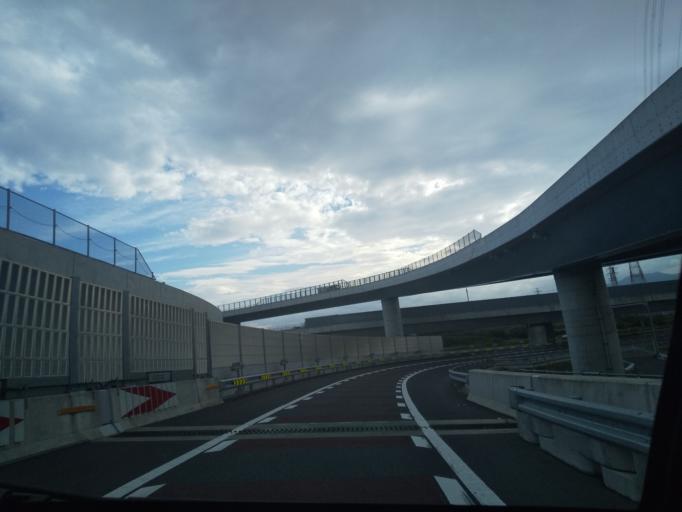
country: JP
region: Kanagawa
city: Atsugi
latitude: 35.4078
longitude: 139.3741
